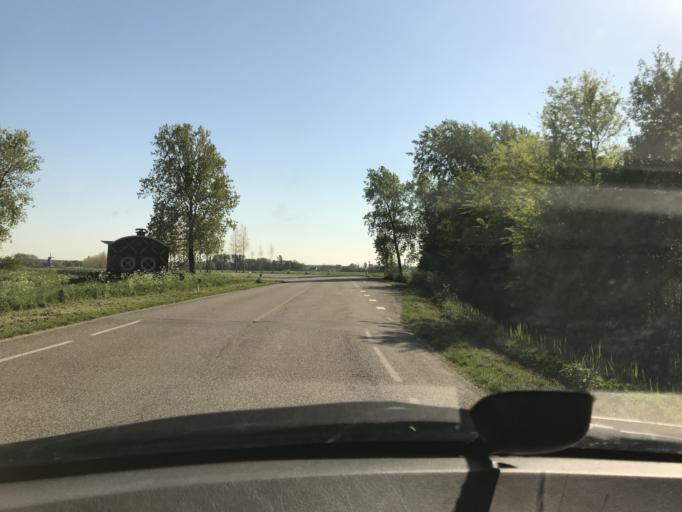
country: NL
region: Zeeland
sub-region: Gemeente Noord-Beveland
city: Kamperland
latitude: 51.5730
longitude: 3.8046
